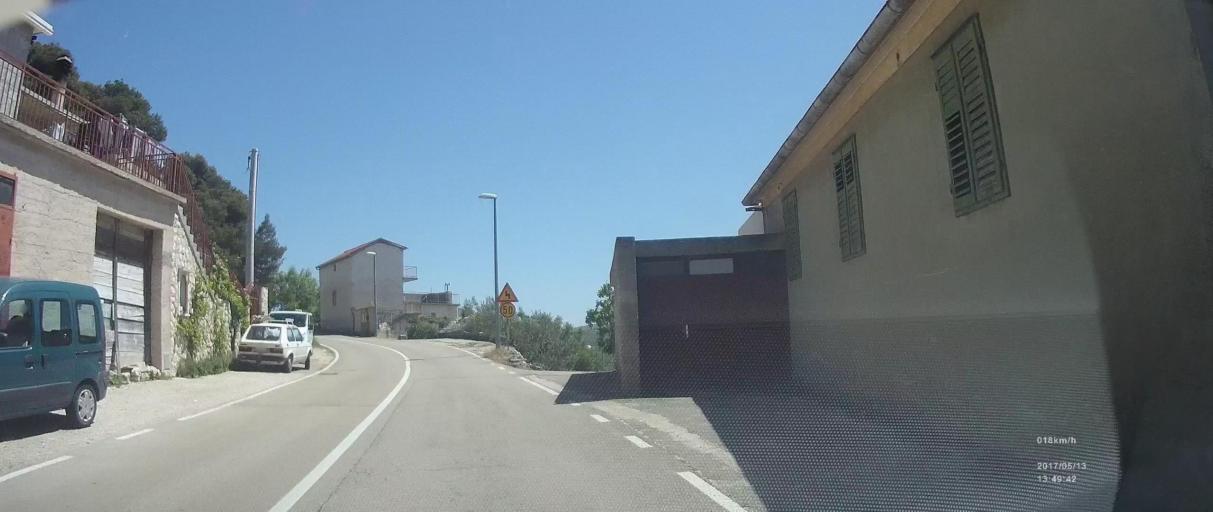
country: HR
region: Sibensko-Kniniska
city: Primosten
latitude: 43.6119
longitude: 15.9776
